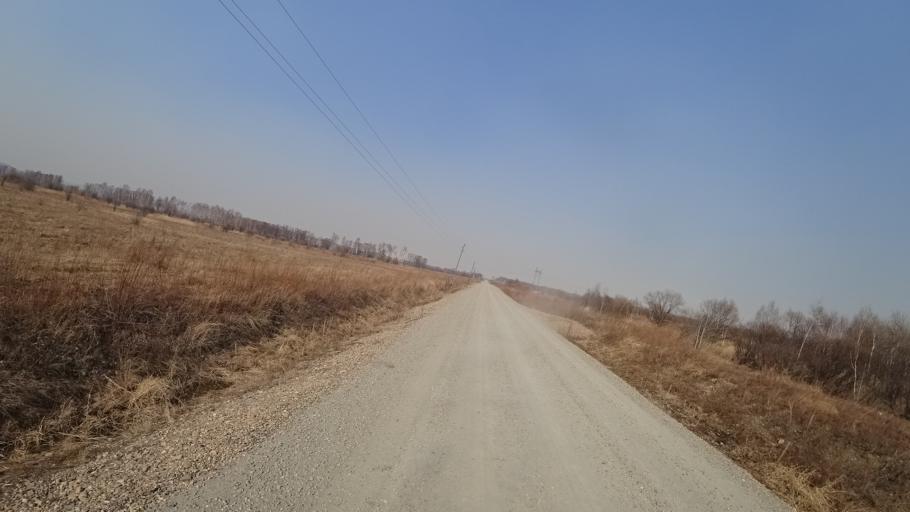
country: RU
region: Amur
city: Novobureyskiy
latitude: 49.8113
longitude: 129.9700
